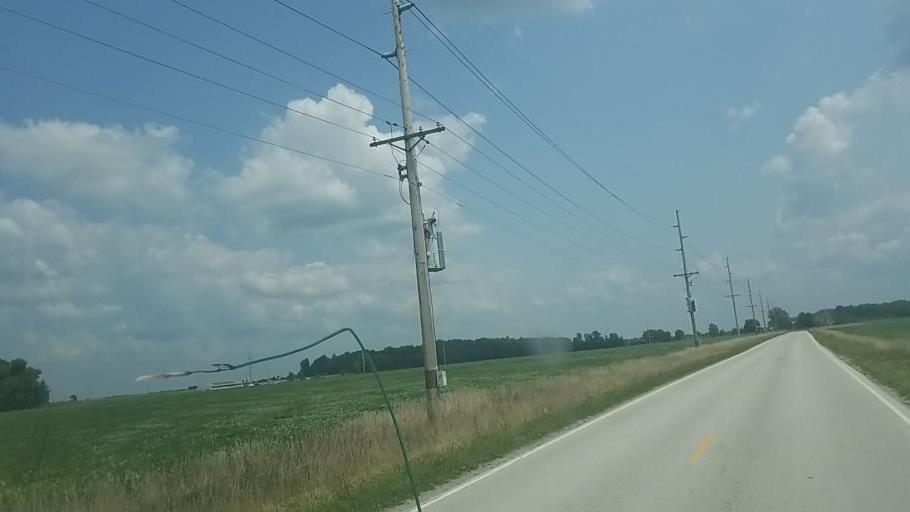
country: US
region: Ohio
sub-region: Wyandot County
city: Carey
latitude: 40.9636
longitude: -83.3102
